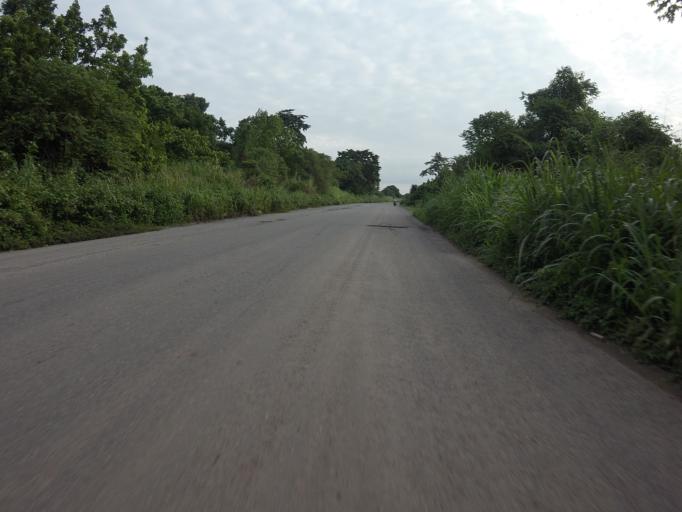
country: GH
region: Volta
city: Kpandu
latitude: 6.8702
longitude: 0.4170
